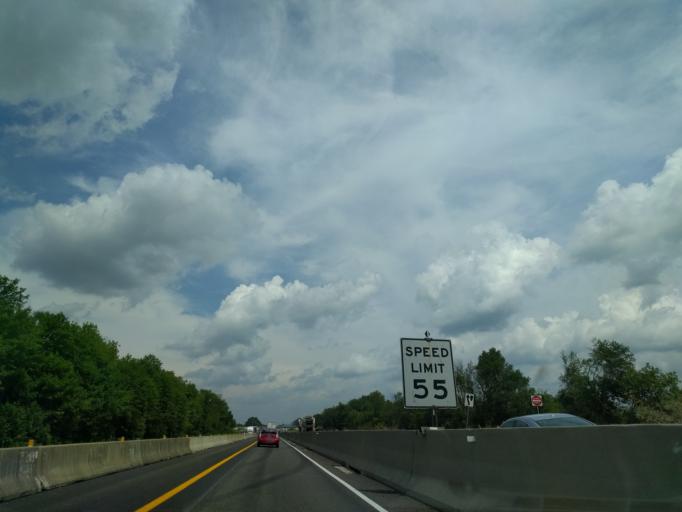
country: US
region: Kentucky
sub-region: Hardin County
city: Elizabethtown
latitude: 37.5650
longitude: -85.8755
